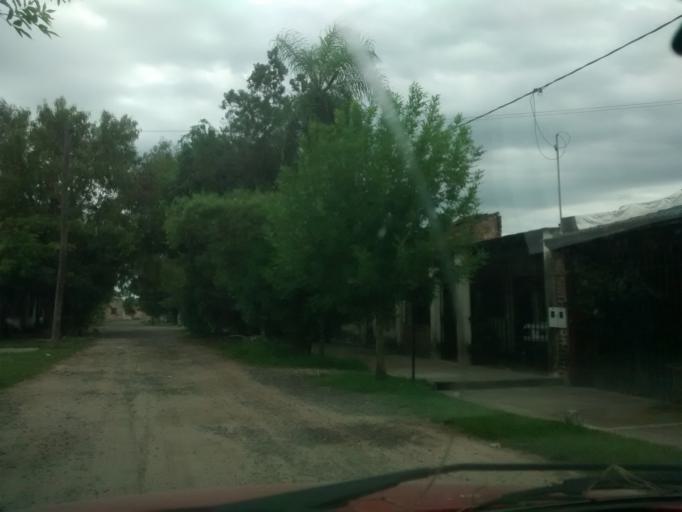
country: AR
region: Chaco
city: Resistencia
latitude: -27.4270
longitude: -58.9758
